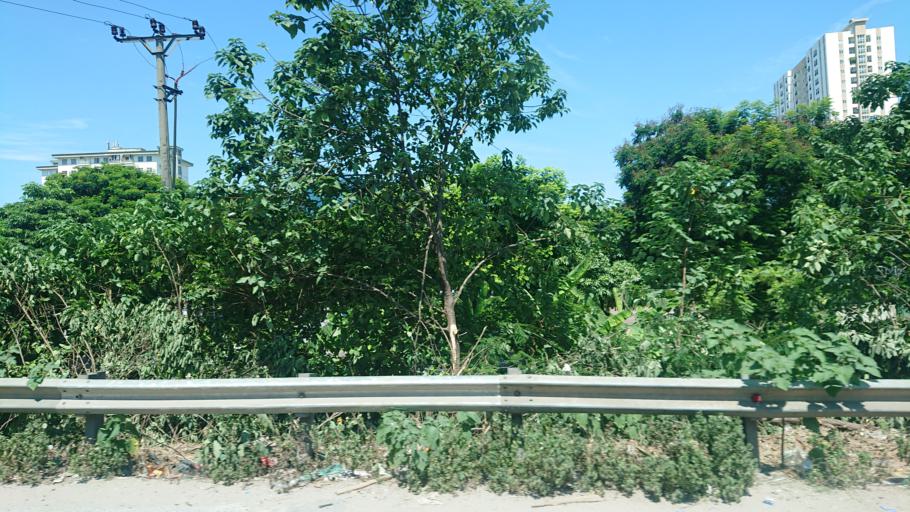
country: VN
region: Ha Noi
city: Van Dien
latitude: 20.9618
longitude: 105.8472
